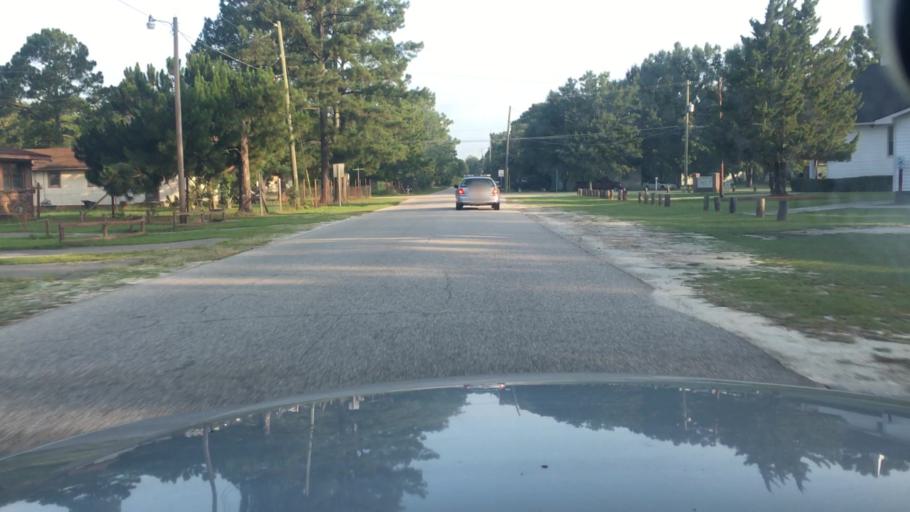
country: US
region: North Carolina
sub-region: Cumberland County
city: Spring Lake
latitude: 35.1138
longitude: -78.9380
